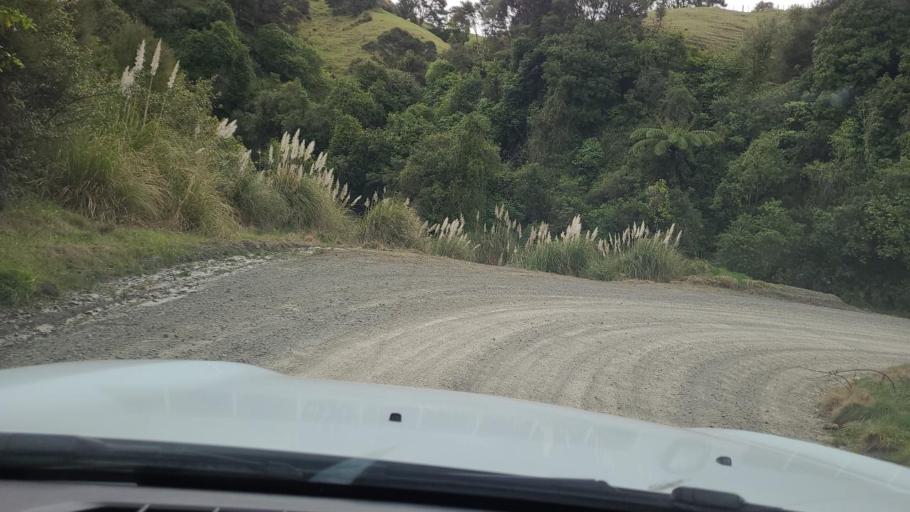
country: NZ
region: Hawke's Bay
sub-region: Napier City
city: Napier
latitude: -39.2929
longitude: 176.8356
